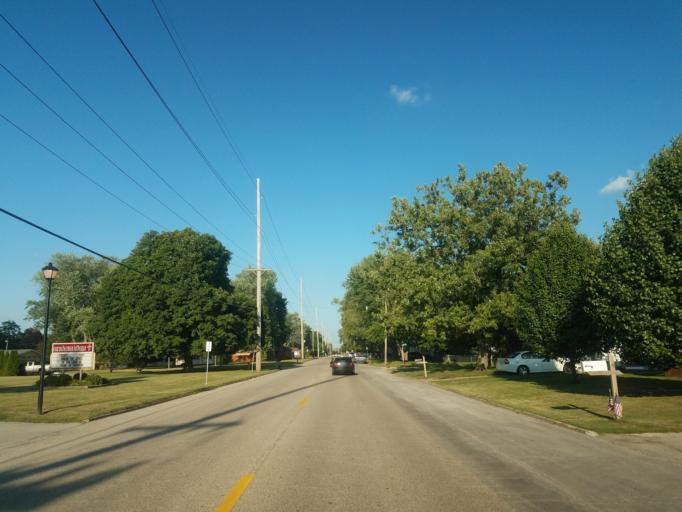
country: US
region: Illinois
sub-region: McLean County
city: Bloomington
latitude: 40.4667
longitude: -88.9697
